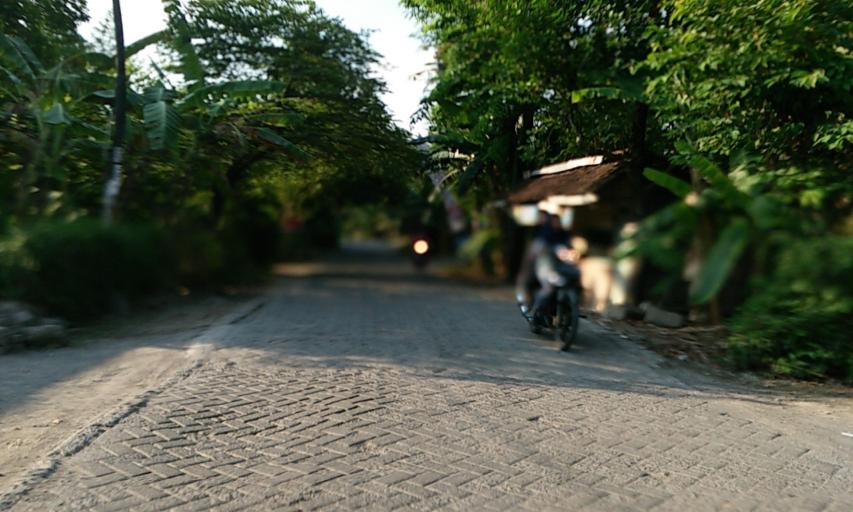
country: ID
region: Central Java
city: Mranggen
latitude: -7.0084
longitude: 110.4883
